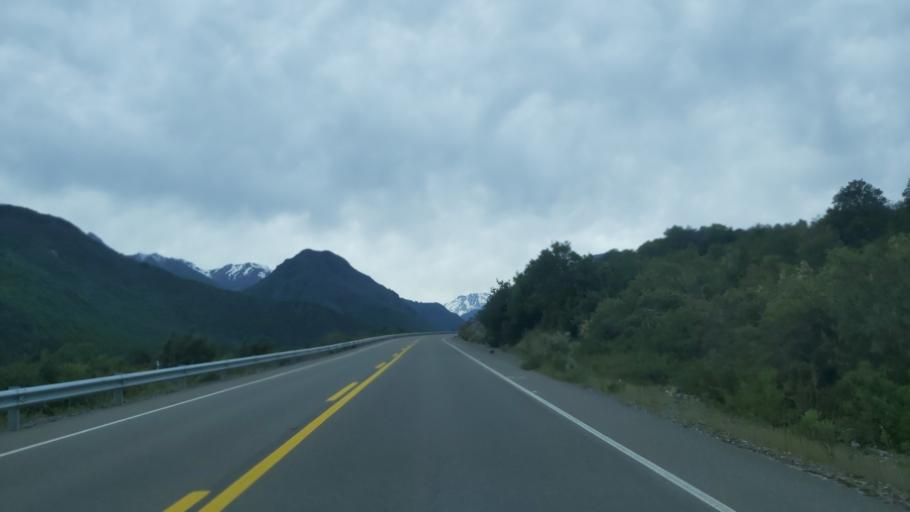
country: CL
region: Maule
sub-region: Provincia de Linares
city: Colbun
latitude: -35.7082
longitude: -71.1036
